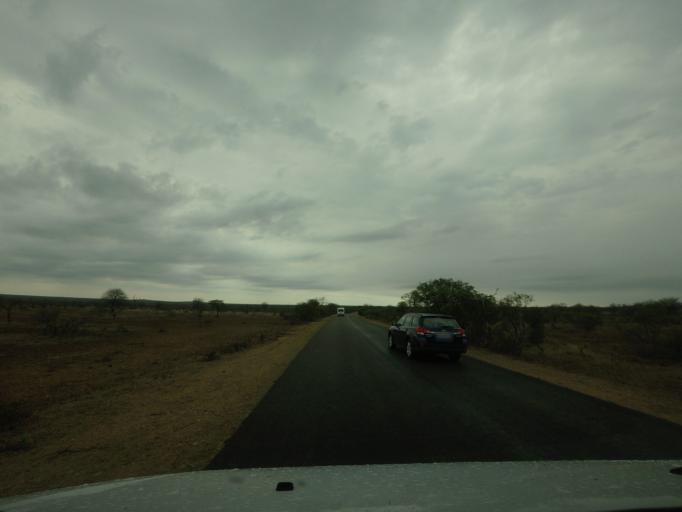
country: ZA
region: Limpopo
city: Thulamahashi
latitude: -24.4736
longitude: 31.4055
